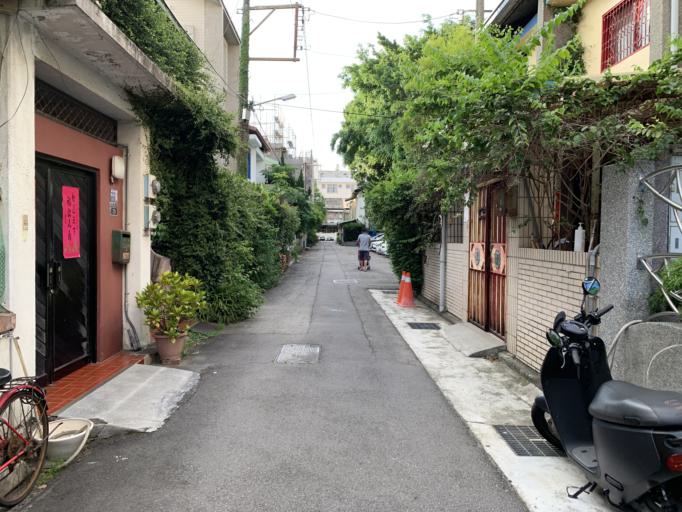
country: TW
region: Taiwan
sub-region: Taichung City
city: Taichung
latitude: 24.1541
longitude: 120.6306
